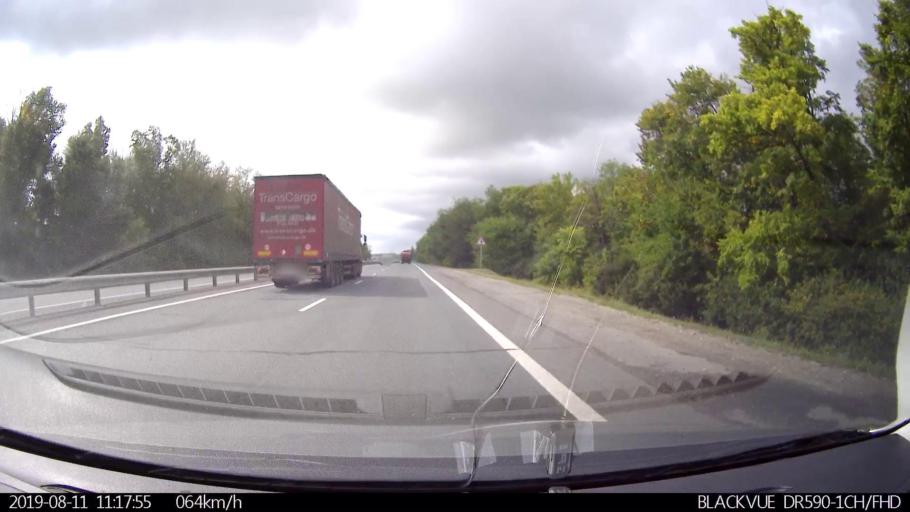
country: RU
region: Ulyanovsk
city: Novoul'yanovsk
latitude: 54.1845
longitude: 48.2727
